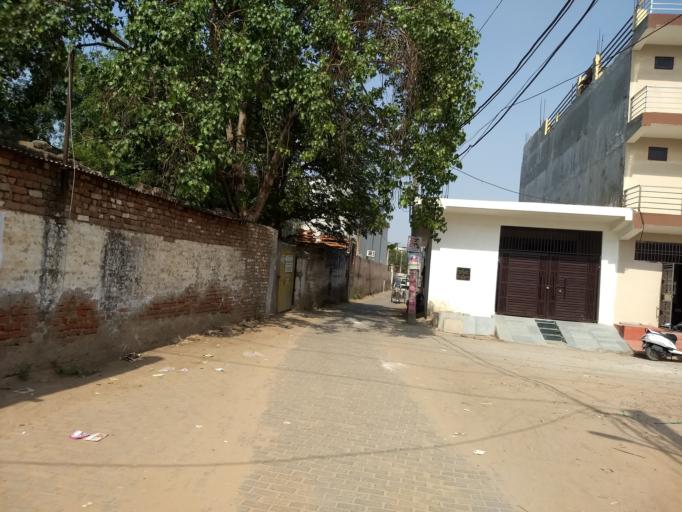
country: IN
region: Haryana
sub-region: Gurgaon
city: Gurgaon
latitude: 28.4485
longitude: 77.0443
